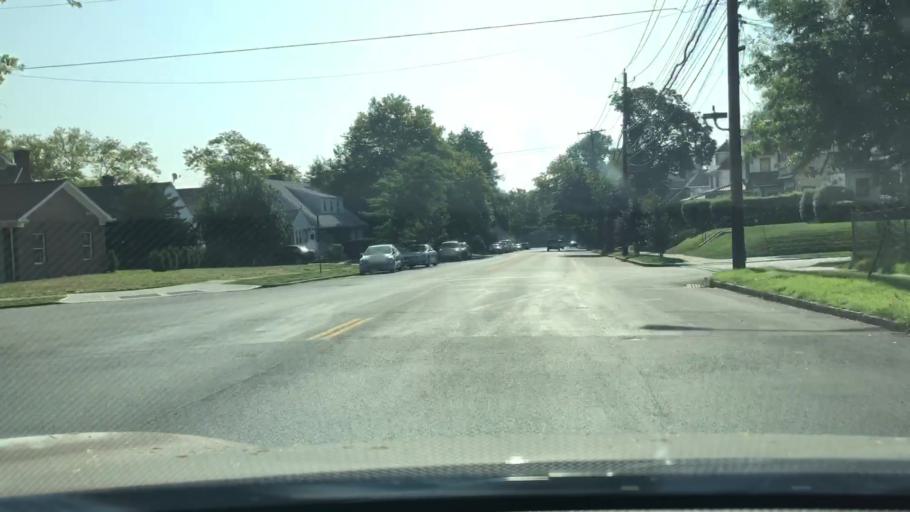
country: US
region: New York
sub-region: Westchester County
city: Pelham
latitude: 40.9176
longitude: -73.8187
